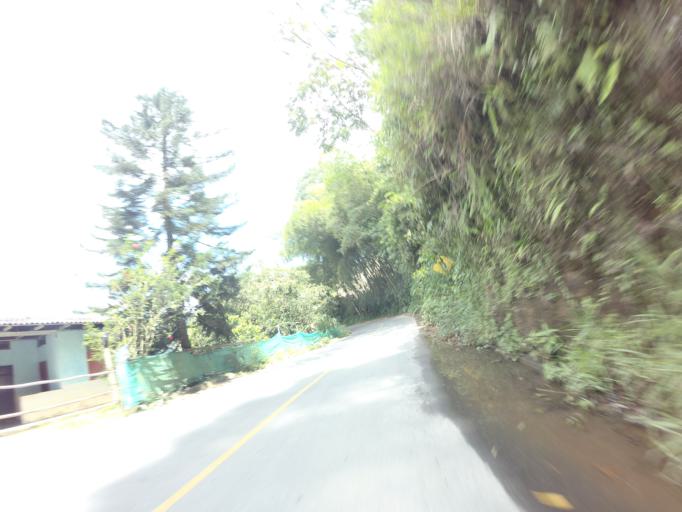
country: CO
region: Caldas
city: Marquetalia
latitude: 5.2978
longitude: -75.0393
